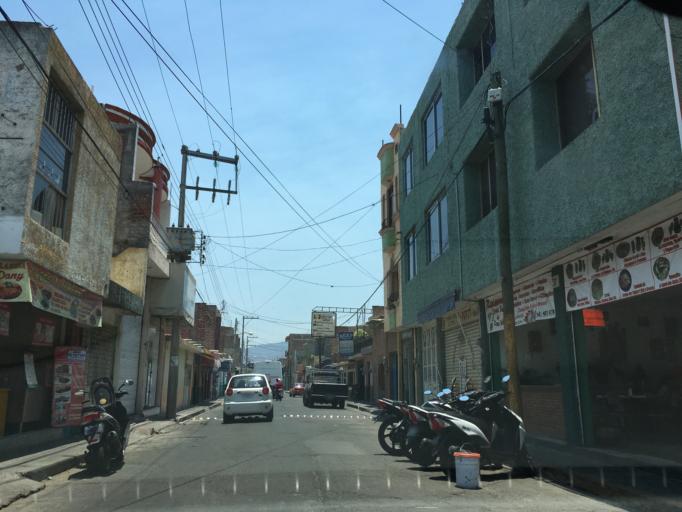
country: MX
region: Guanajuato
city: Uriangato
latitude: 20.1371
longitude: -101.1825
